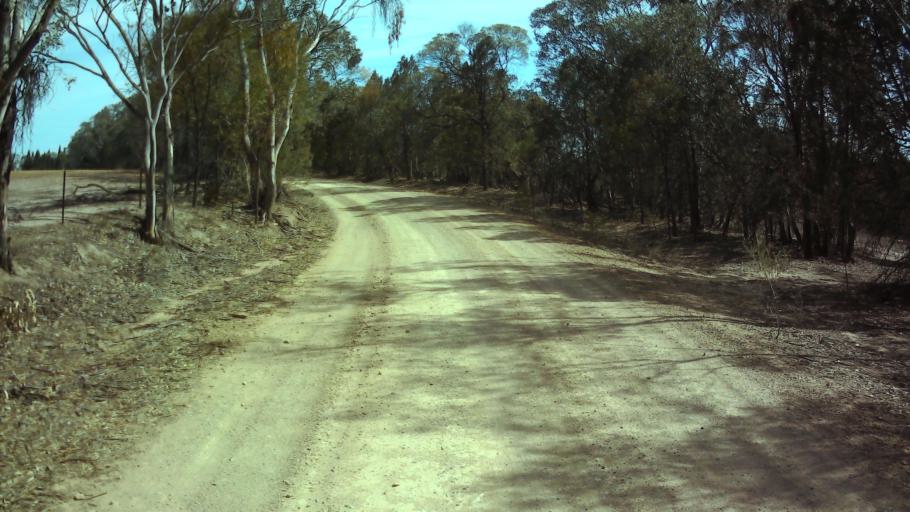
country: AU
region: New South Wales
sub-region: Weddin
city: Grenfell
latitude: -33.8821
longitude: 148.1511
